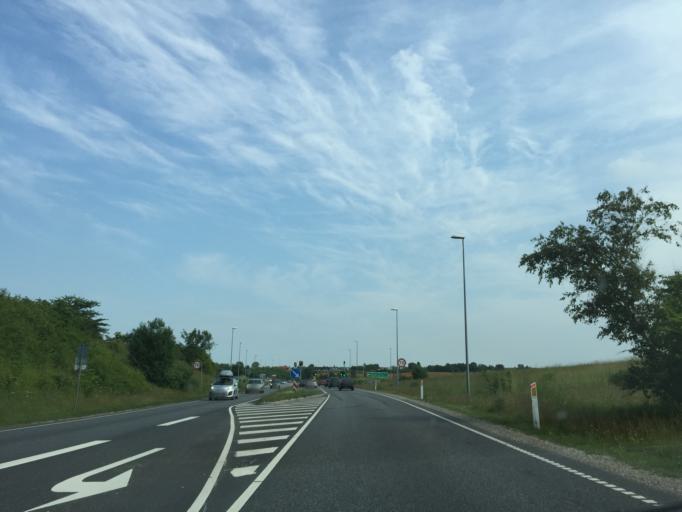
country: DK
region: Central Jutland
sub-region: Arhus Kommune
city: Sabro
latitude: 56.1910
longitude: 10.0732
